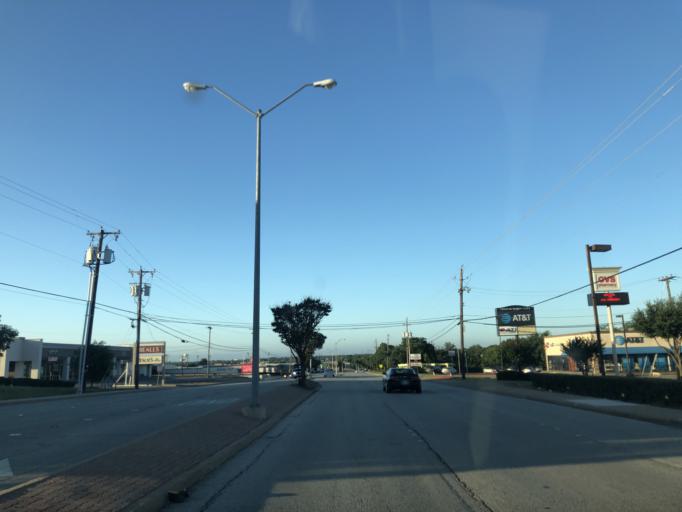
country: US
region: Texas
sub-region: Dallas County
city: Duncanville
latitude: 32.6473
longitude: -96.9255
